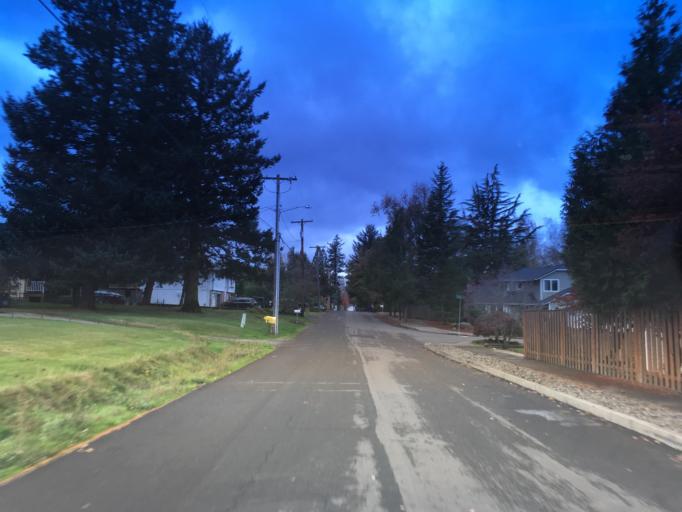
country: US
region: Oregon
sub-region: Multnomah County
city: Fairview
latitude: 45.5394
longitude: -122.4300
